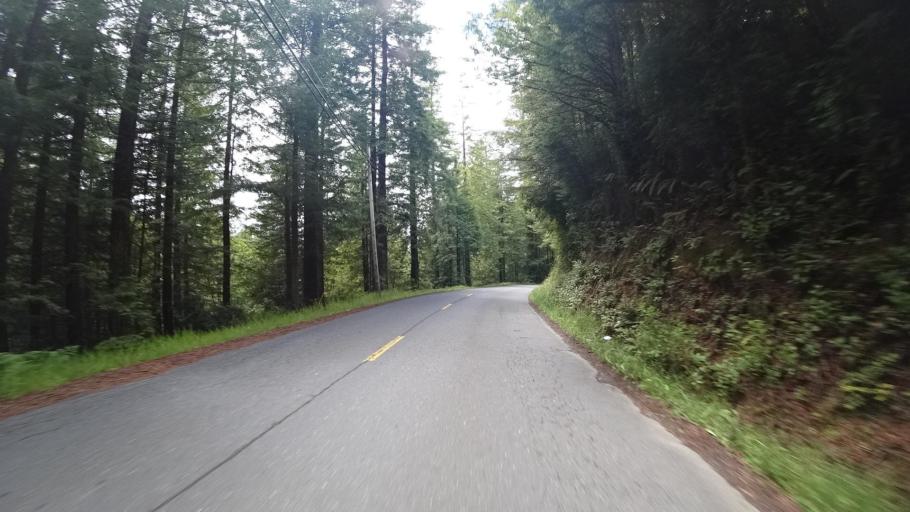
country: US
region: California
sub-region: Humboldt County
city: Bayside
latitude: 40.7871
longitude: -124.0732
